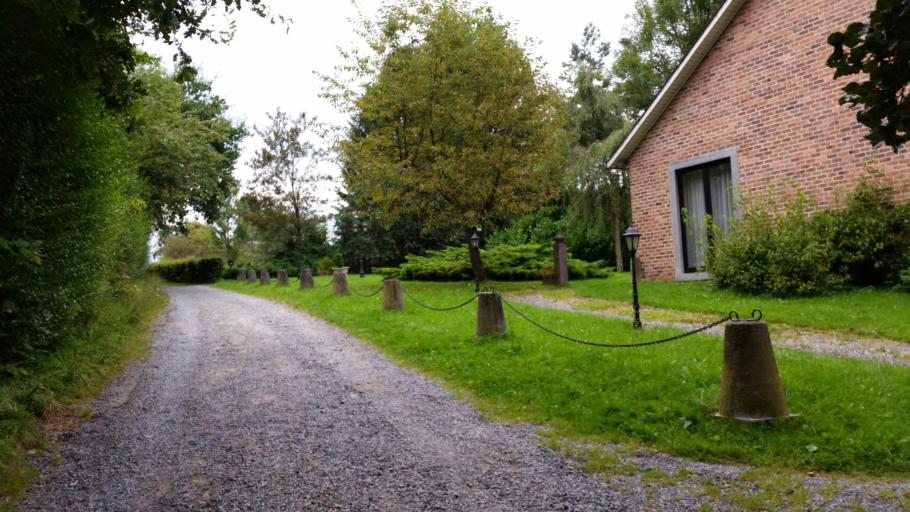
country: BE
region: Wallonia
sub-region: Province du Luxembourg
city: Durbuy
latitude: 50.3516
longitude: 5.4606
